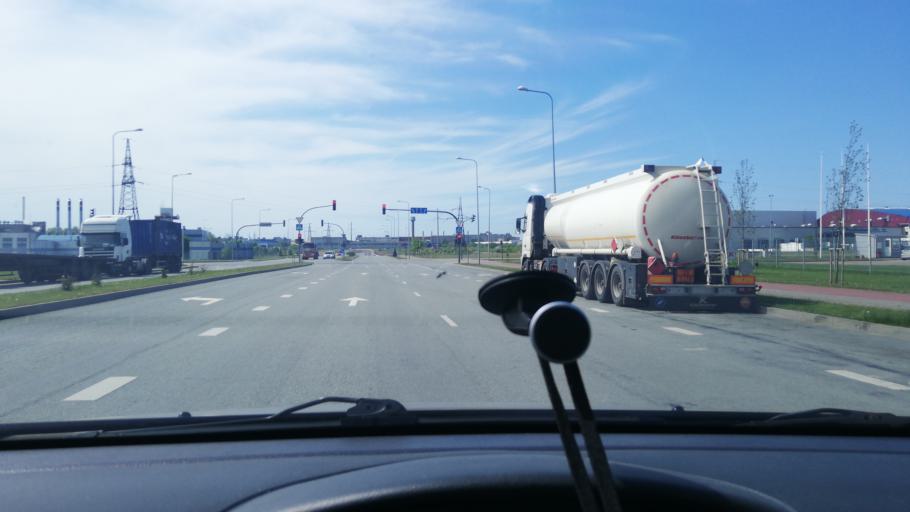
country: LT
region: Klaipedos apskritis
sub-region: Klaipeda
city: Klaipeda
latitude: 55.6868
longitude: 21.2066
